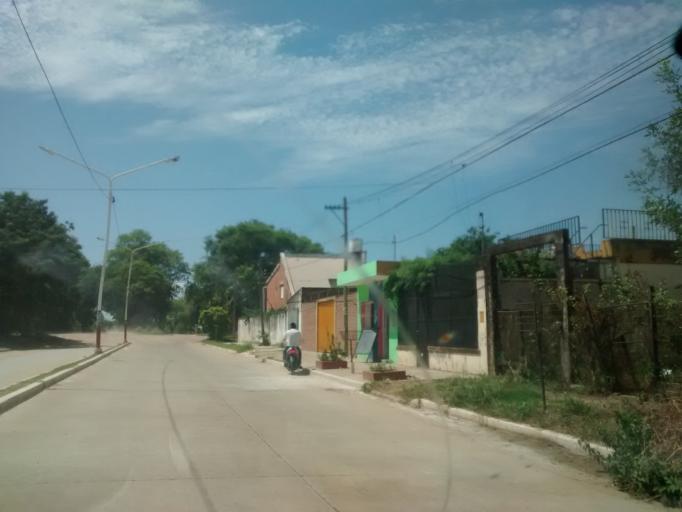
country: AR
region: Chaco
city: Resistencia
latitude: -27.4442
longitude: -58.9656
